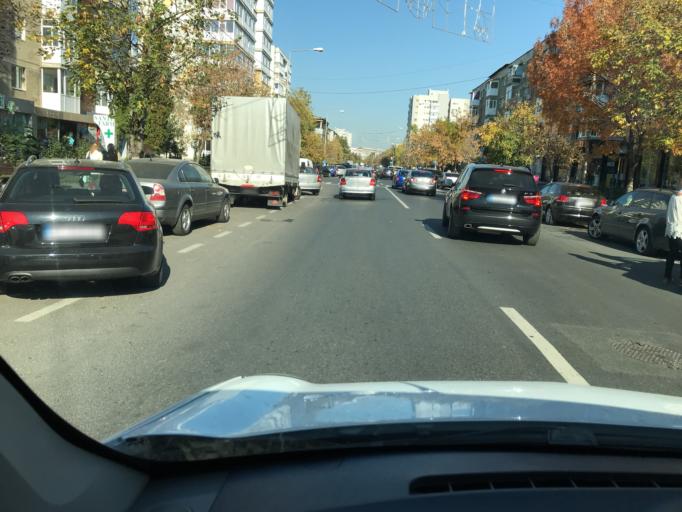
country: RO
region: Olt
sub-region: Municipiul Slatina
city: Slatina
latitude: 44.4306
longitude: 24.3734
